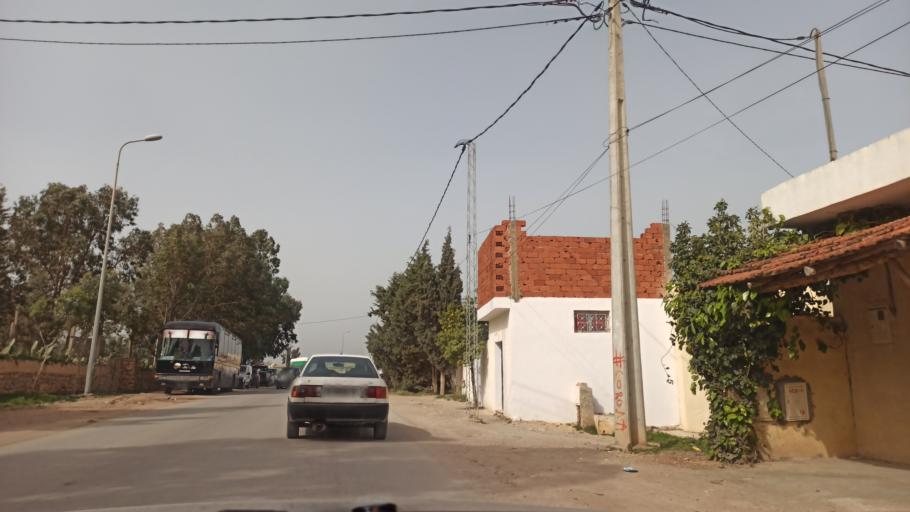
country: TN
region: Zaghwan
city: Zaghouan
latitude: 36.4163
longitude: 10.1243
